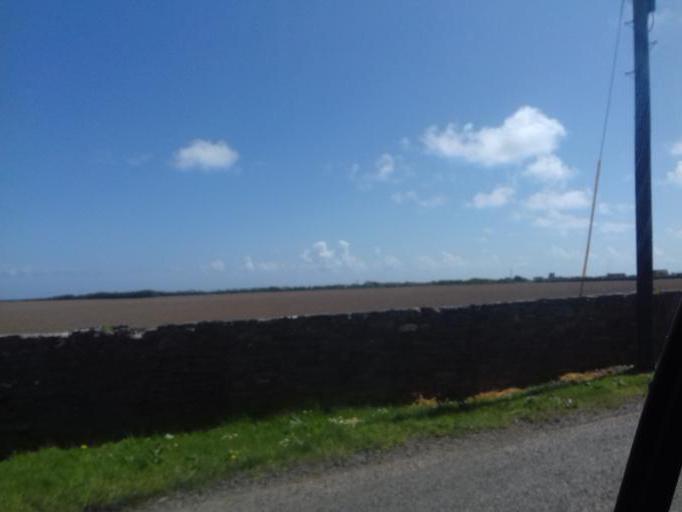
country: IE
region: Munster
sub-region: Waterford
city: Dunmore East
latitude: 52.1408
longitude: -6.9128
